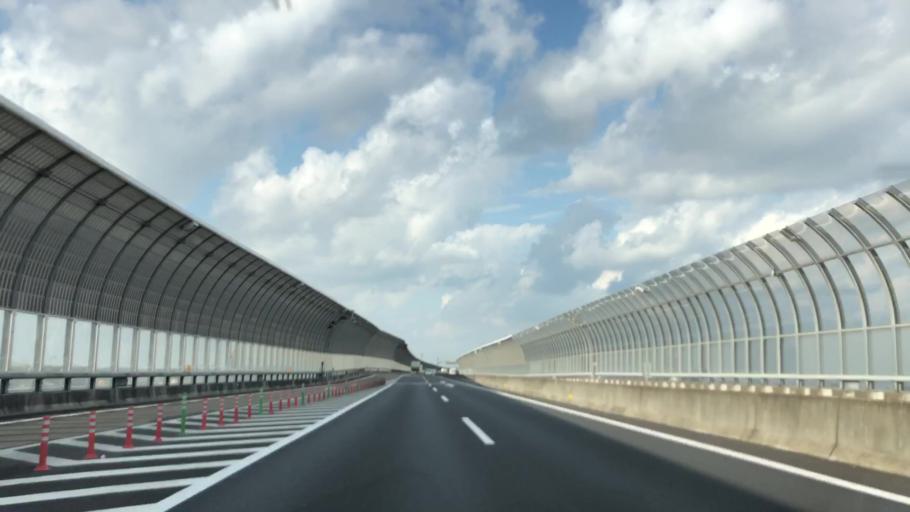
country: JP
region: Chiba
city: Matsudo
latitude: 35.8046
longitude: 139.8770
